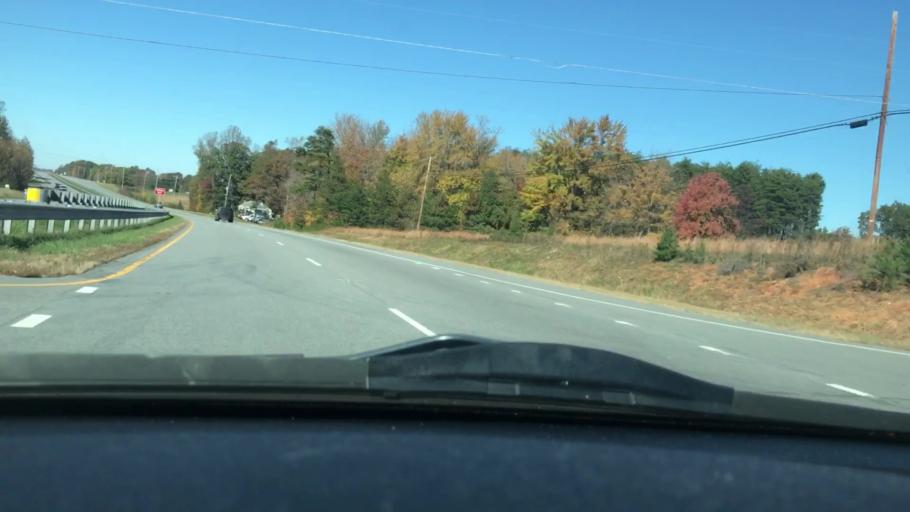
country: US
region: North Carolina
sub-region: Rockingham County
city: Madison
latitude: 36.3402
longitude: -79.9434
